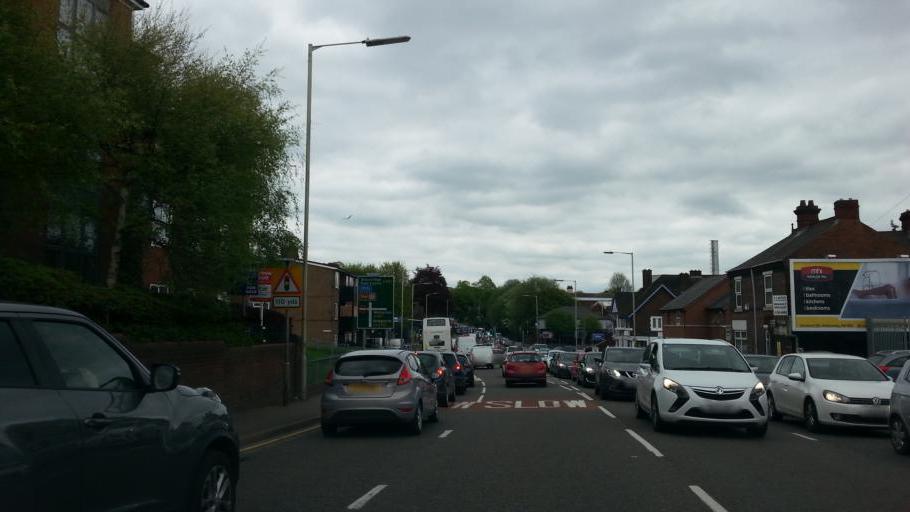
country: GB
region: England
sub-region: Dudley
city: Stourbridge
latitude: 52.4690
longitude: -2.1541
